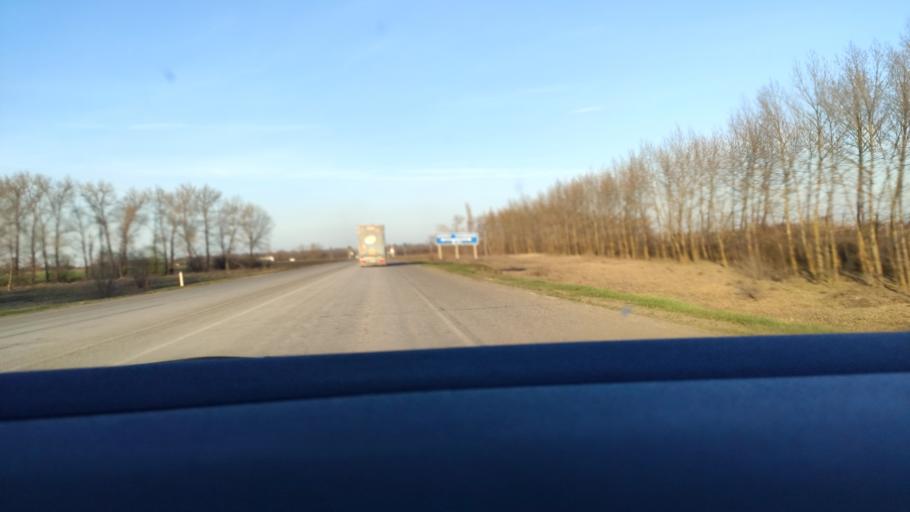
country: RU
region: Voronezj
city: Novovoronezh
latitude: 51.4215
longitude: 39.2930
